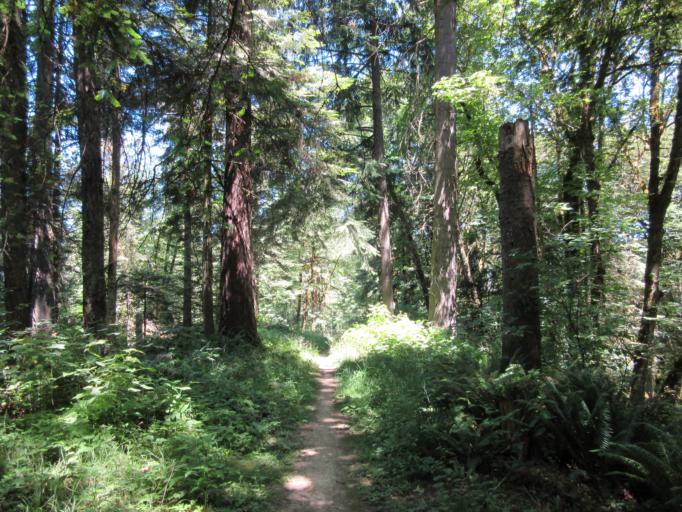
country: US
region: Oregon
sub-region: Washington County
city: West Haven
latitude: 45.5591
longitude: -122.7493
